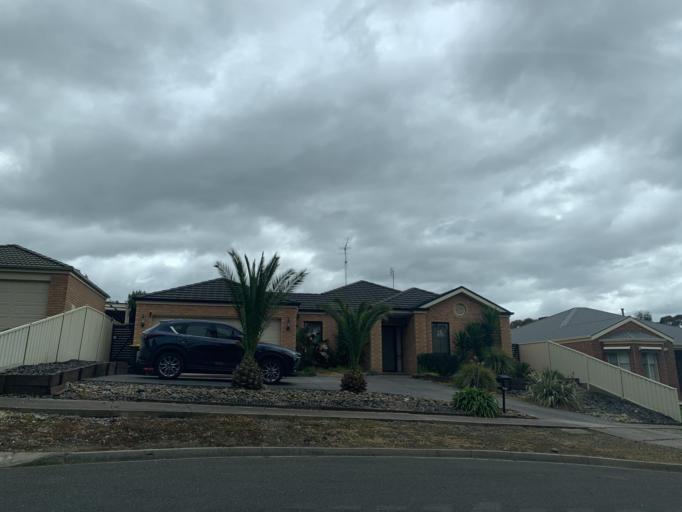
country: AU
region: Victoria
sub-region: Whittlesea
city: Whittlesea
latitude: -37.2128
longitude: 145.0427
